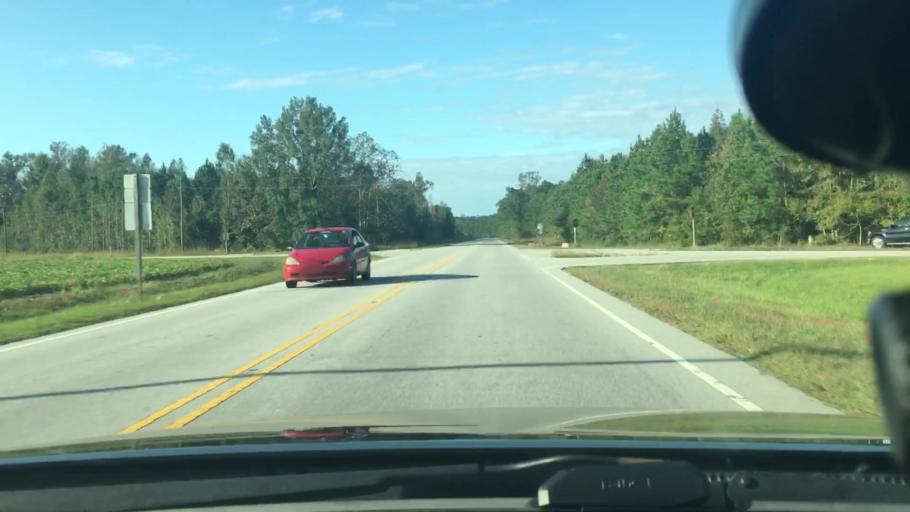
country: US
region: North Carolina
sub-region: Craven County
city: Vanceboro
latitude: 35.2946
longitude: -77.1304
